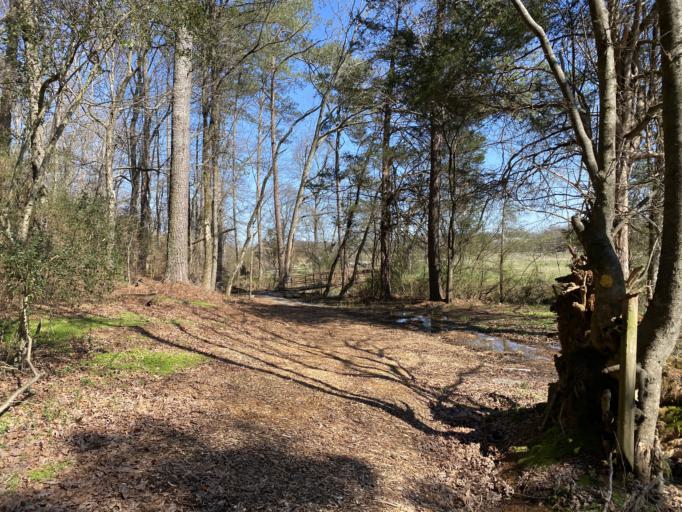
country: US
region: Georgia
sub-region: Gordon County
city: Calhoun
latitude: 34.4630
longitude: -84.9851
